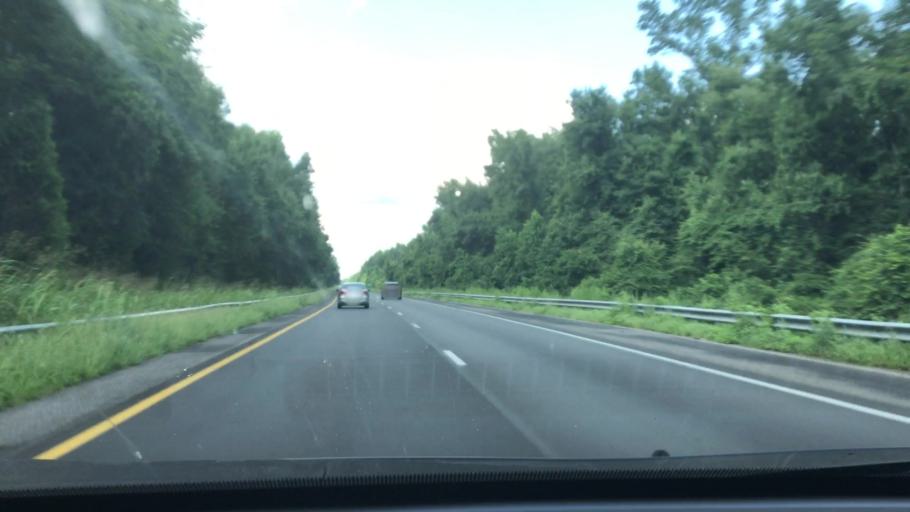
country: US
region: South Carolina
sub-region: Clarendon County
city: Manning
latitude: 33.8238
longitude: -80.1382
